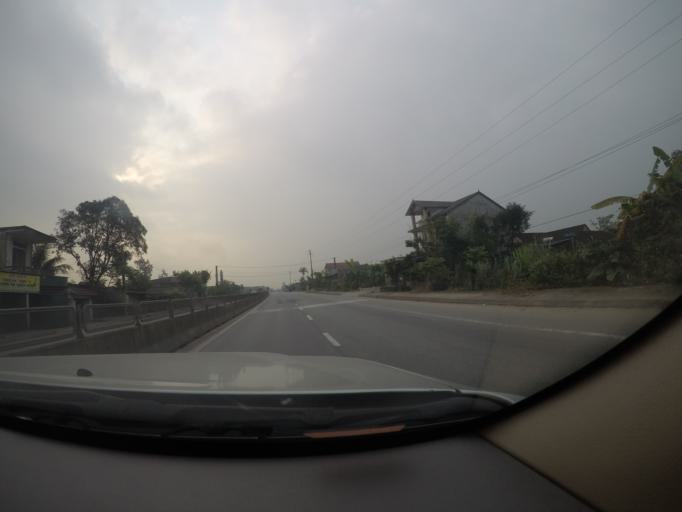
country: VN
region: Ha Tinh
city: Cam Xuyen
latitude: 18.2405
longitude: 106.0154
